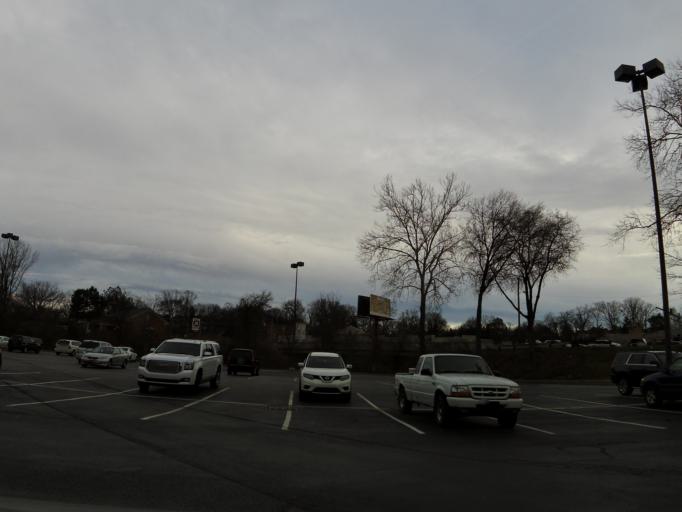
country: US
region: Tennessee
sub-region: Knox County
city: Knoxville
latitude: 35.9419
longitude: -83.9822
